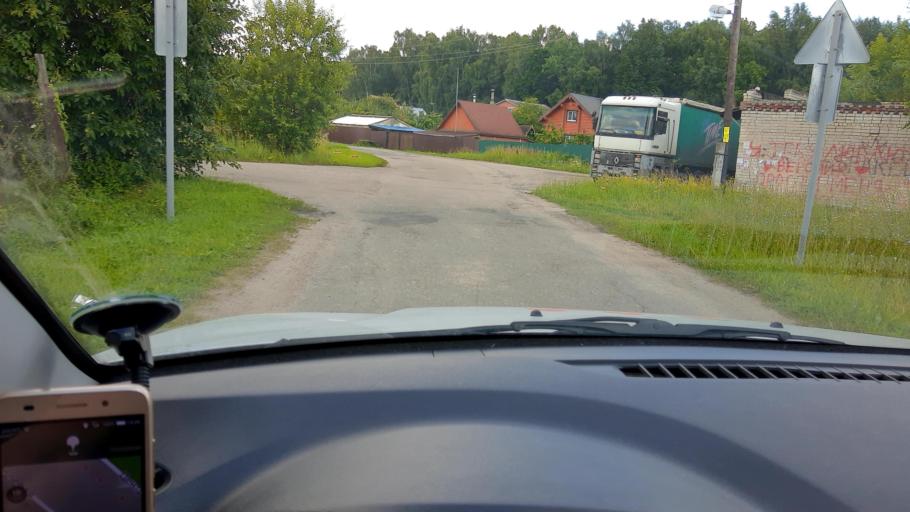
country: RU
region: Nizjnij Novgorod
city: Afonino
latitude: 56.2006
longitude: 44.0296
